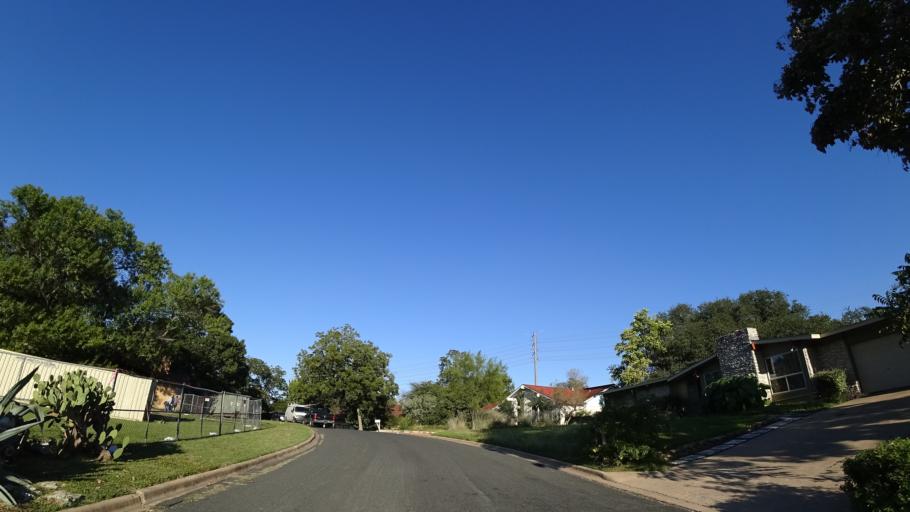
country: US
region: Texas
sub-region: Travis County
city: Austin
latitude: 30.2182
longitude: -97.7361
